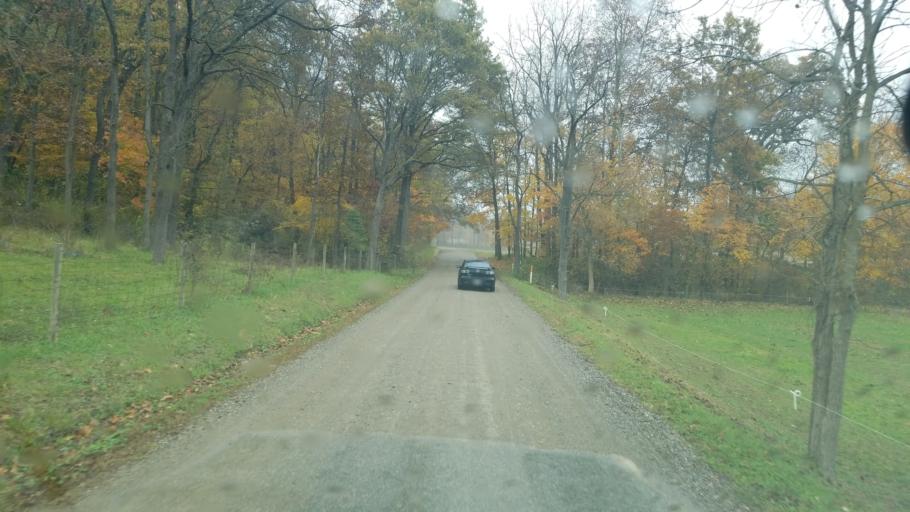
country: US
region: Ohio
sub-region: Holmes County
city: Millersburg
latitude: 40.4554
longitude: -81.8565
